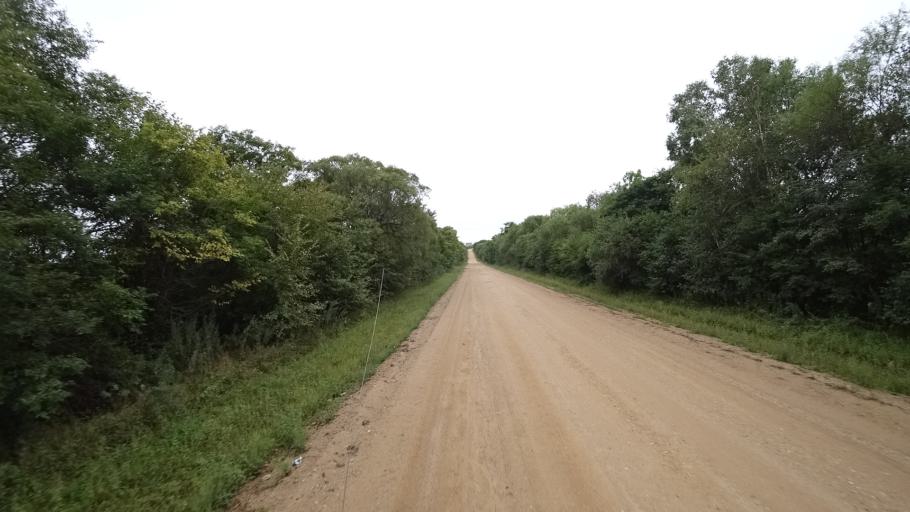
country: RU
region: Primorskiy
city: Monastyrishche
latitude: 44.0873
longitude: 132.5971
